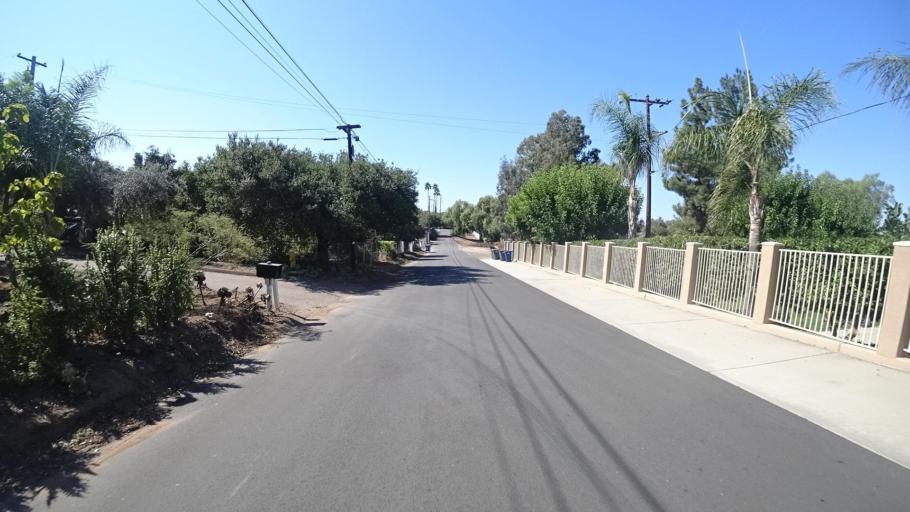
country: US
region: California
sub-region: San Diego County
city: Granite Hills
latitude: 32.7953
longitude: -116.8993
